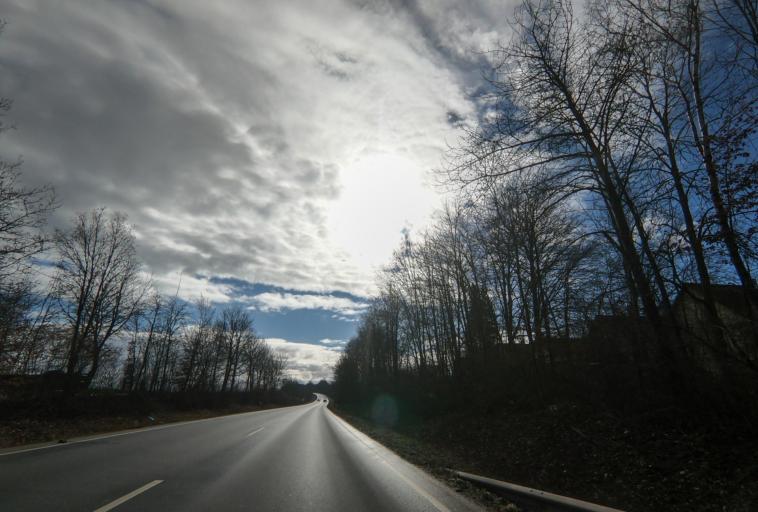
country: DE
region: Bavaria
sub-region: Upper Palatinate
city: Alteglofsheim
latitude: 48.9192
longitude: 12.2097
